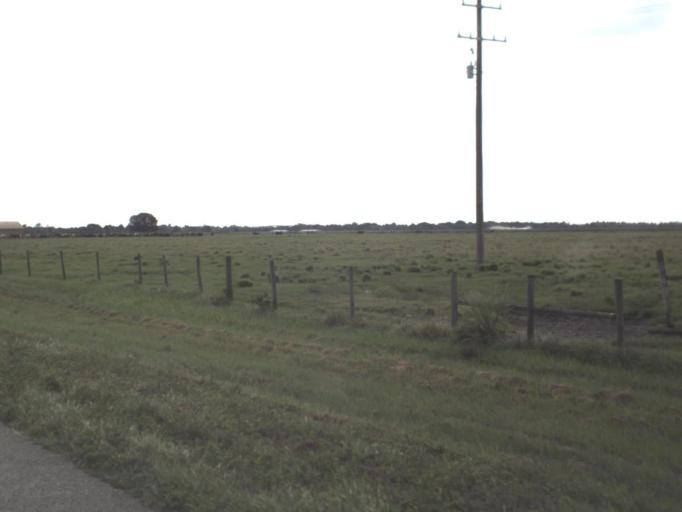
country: US
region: Florida
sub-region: Okeechobee County
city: Cypress Quarters
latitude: 27.3834
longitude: -80.8168
